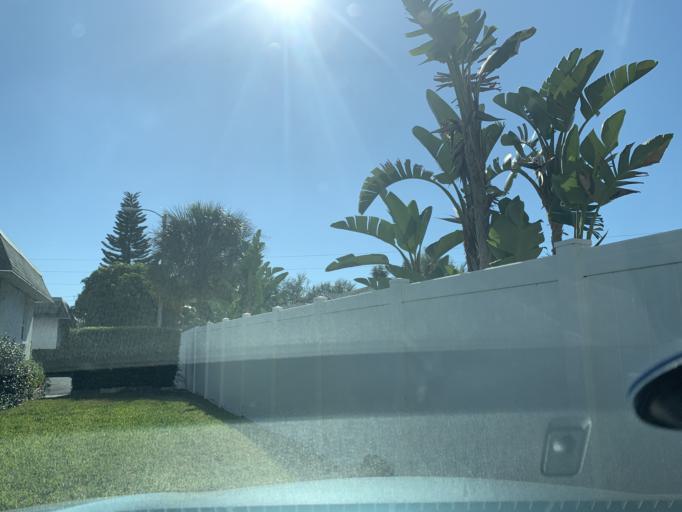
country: US
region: Florida
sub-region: Pinellas County
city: Kenneth City
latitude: 27.8075
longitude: -82.7477
